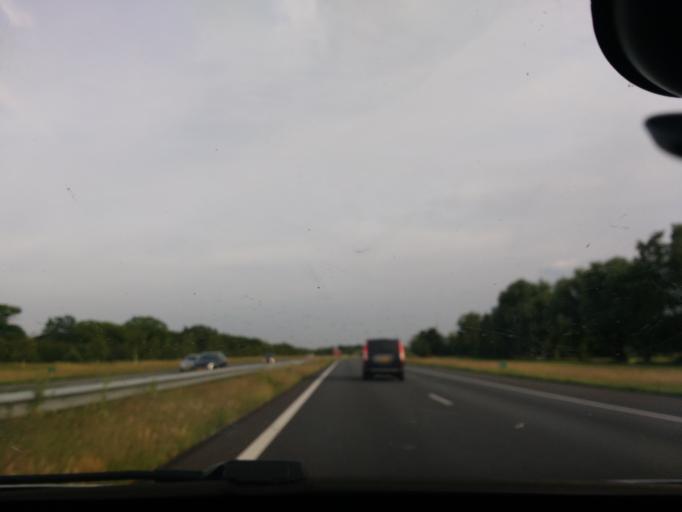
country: NL
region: North Brabant
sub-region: Gemeente Sint-Oedenrode
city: Sint-Oedenrode
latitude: 51.5474
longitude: 5.4810
